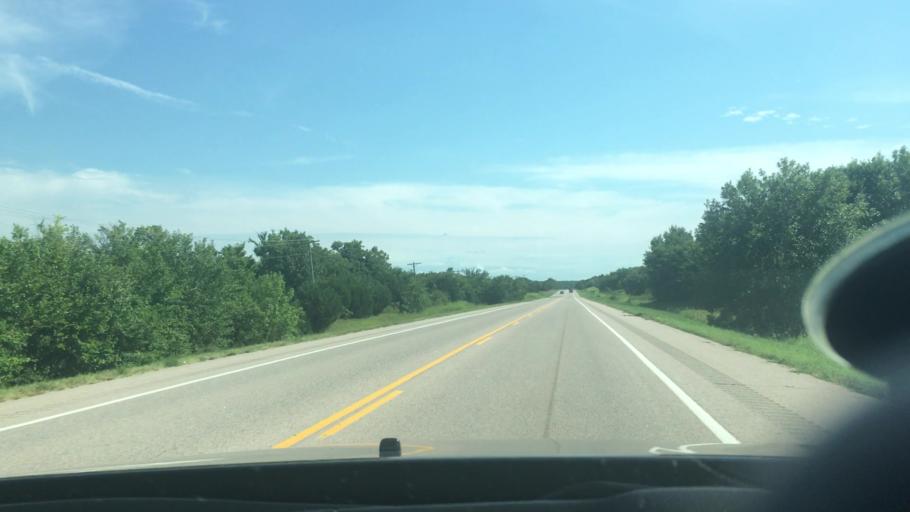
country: US
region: Oklahoma
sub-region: Seminole County
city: Konawa
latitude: 34.9754
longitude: -96.6791
